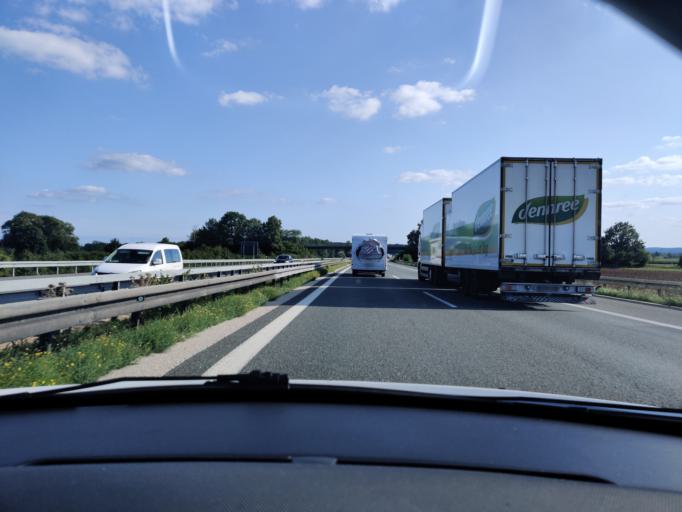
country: DE
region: Bavaria
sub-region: Upper Palatinate
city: Schwarzenfeld
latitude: 49.3750
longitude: 12.1518
